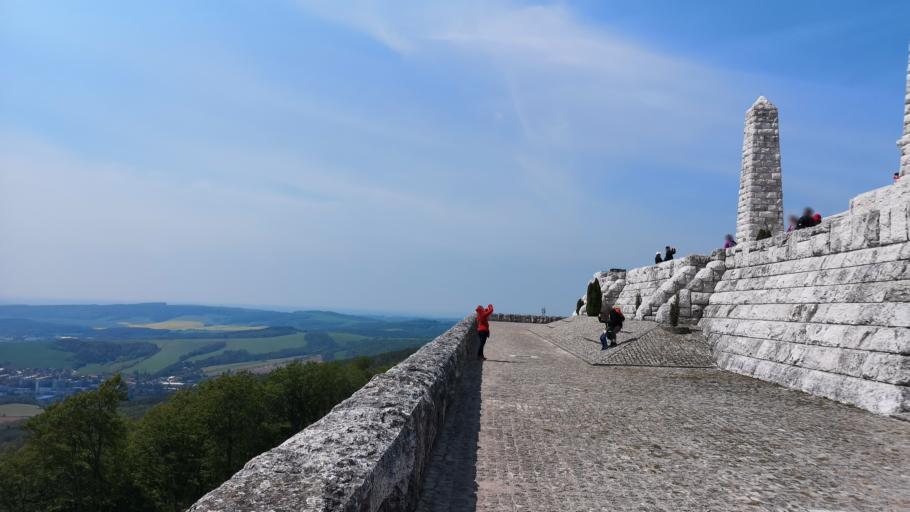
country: SK
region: Nitriansky
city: Brezova pod Bradlom
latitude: 48.6792
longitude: 17.5642
